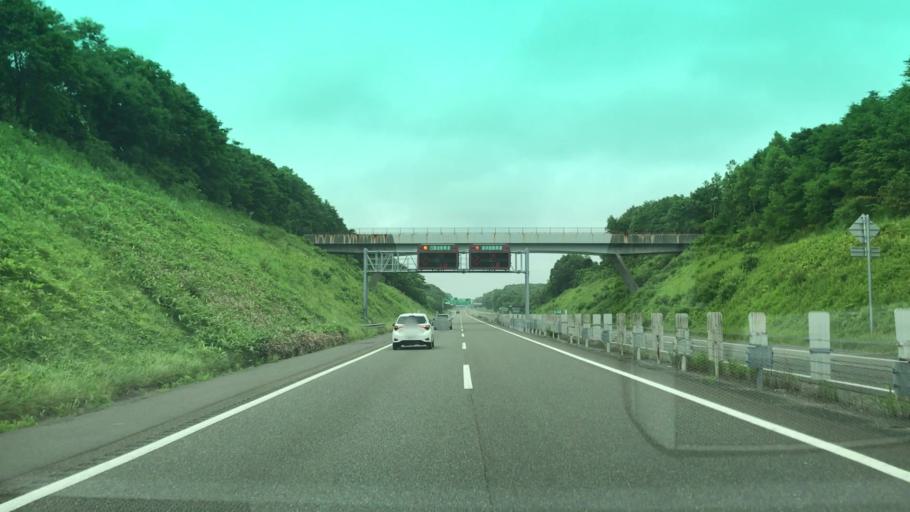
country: JP
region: Hokkaido
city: Tomakomai
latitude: 42.7021
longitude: 141.6517
